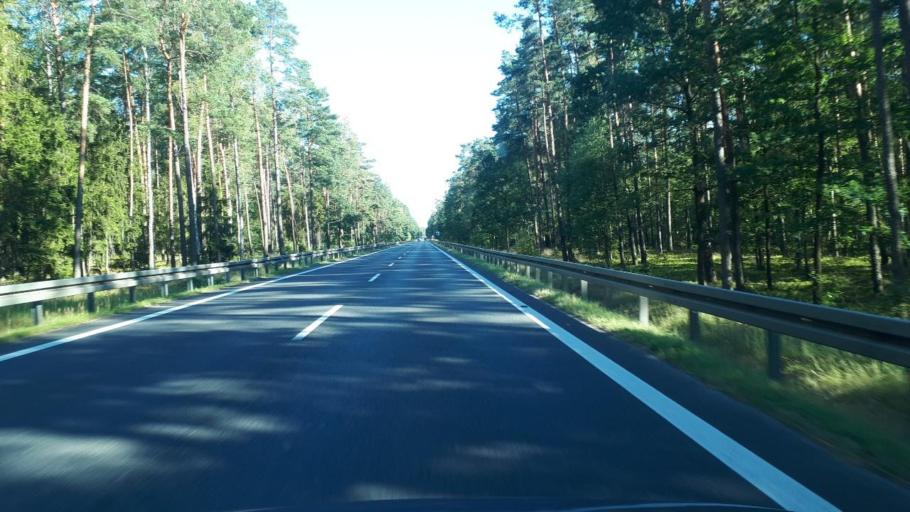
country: PL
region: Silesian Voivodeship
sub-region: Powiat lubliniecki
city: Lubliniec
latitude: 50.6164
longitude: 18.6894
